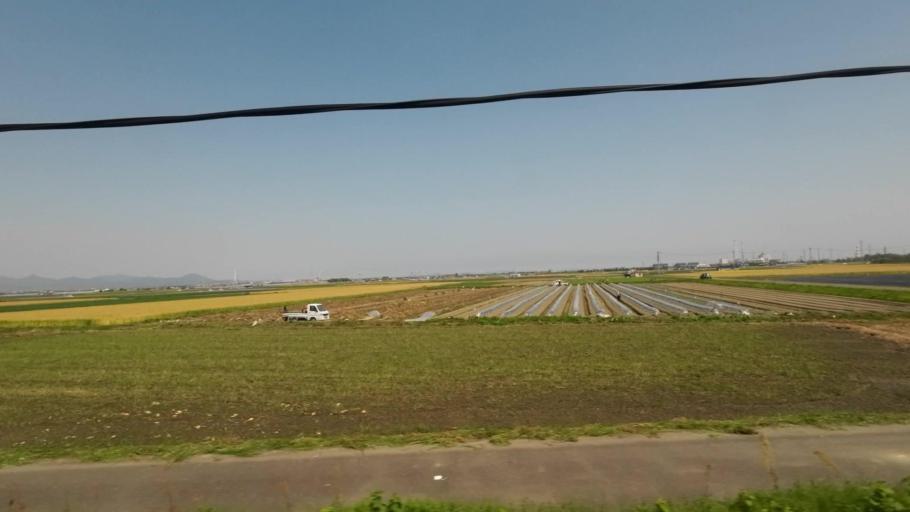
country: JP
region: Ehime
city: Saijo
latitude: 33.8966
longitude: 133.1641
